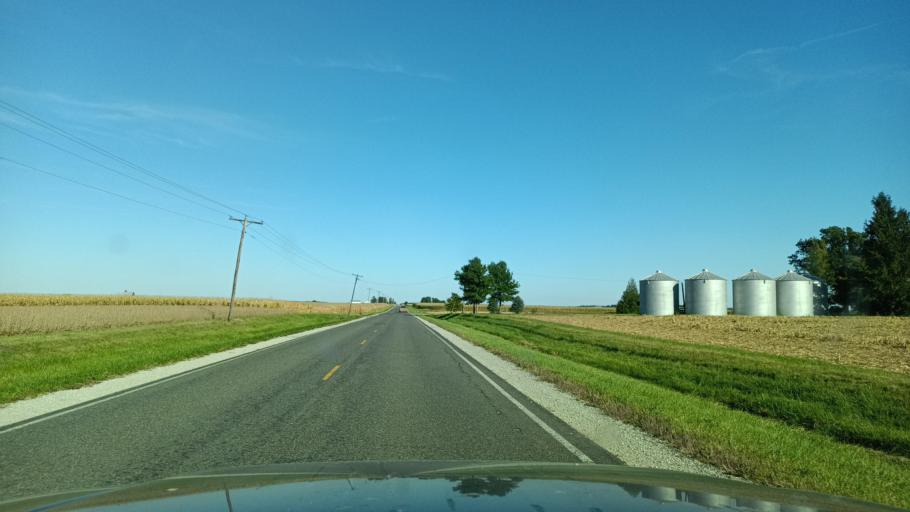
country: US
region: Illinois
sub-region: De Witt County
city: Clinton
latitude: 40.2244
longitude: -88.8912
